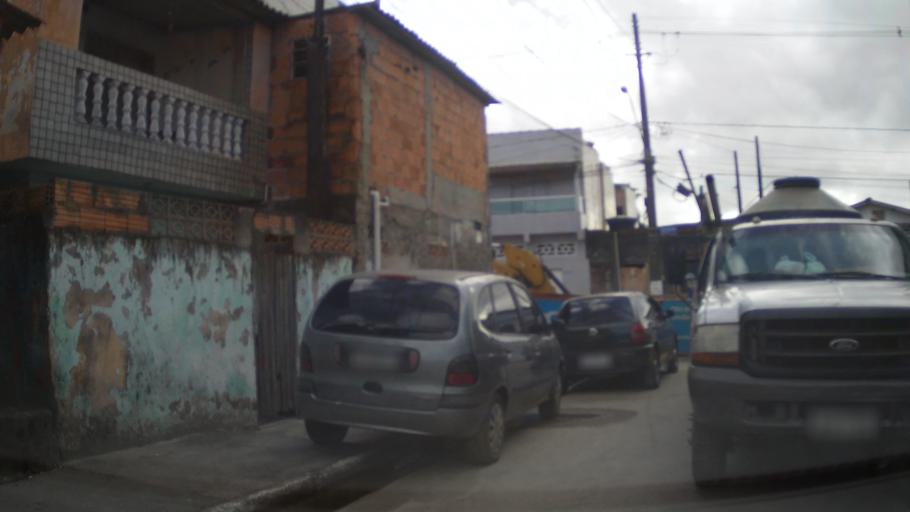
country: BR
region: Sao Paulo
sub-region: Praia Grande
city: Praia Grande
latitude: -24.0142
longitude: -46.4716
